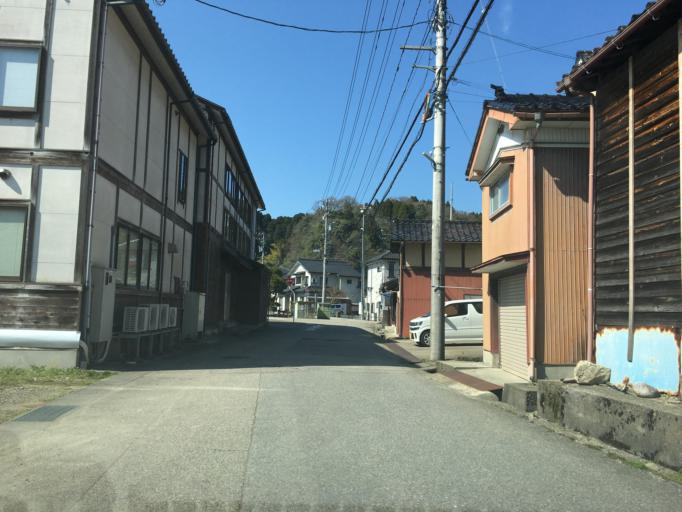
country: JP
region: Toyama
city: Himi
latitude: 36.8901
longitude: 137.0003
